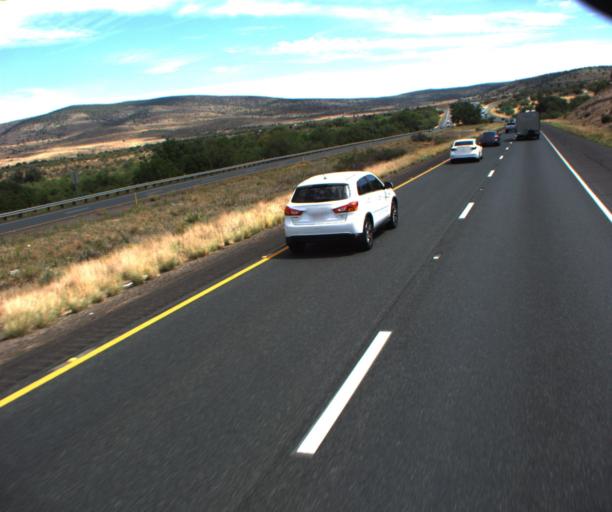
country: US
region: Arizona
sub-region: Yavapai County
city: Camp Verde
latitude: 34.5053
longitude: -111.9989
